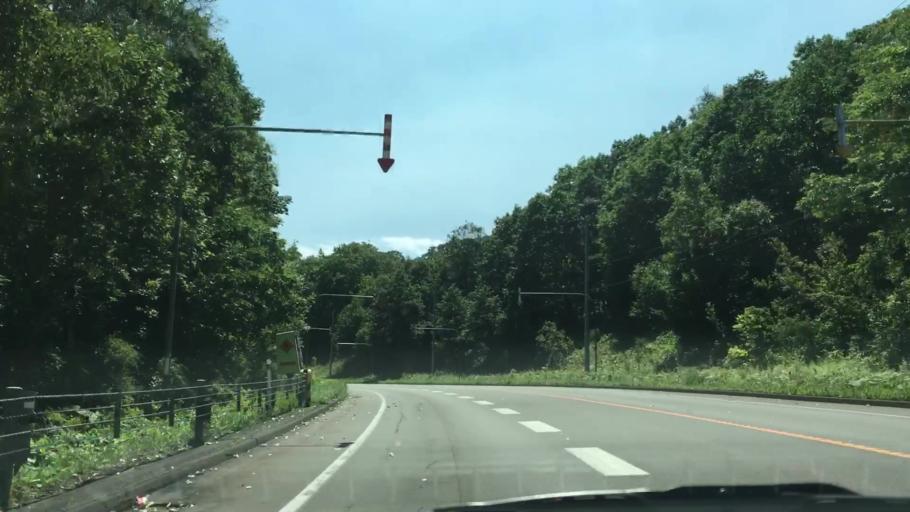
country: JP
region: Hokkaido
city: Otofuke
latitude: 43.2323
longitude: 143.5260
